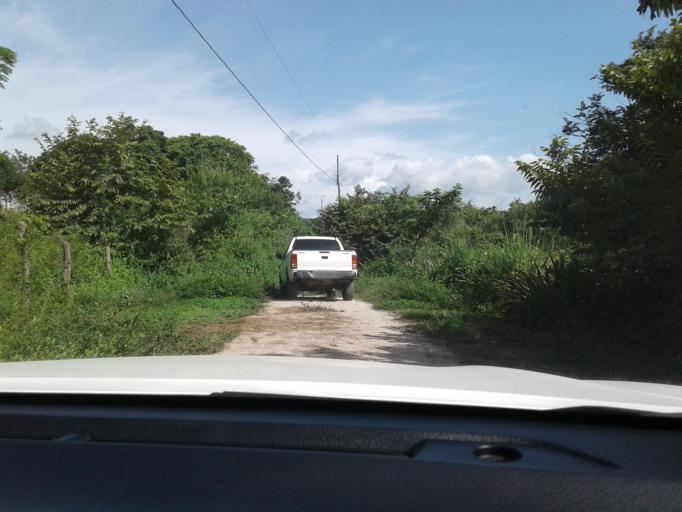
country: NI
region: Matagalpa
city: Terrabona
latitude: 12.5573
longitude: -86.0196
